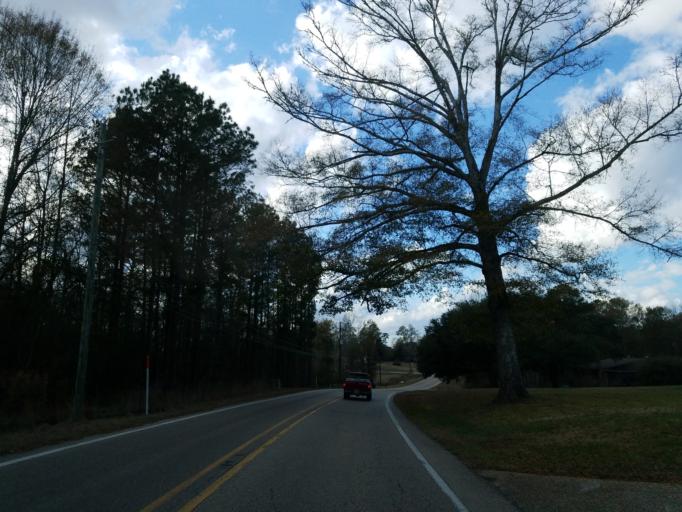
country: US
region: Mississippi
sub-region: Jones County
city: Ellisville
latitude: 31.5941
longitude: -89.1923
